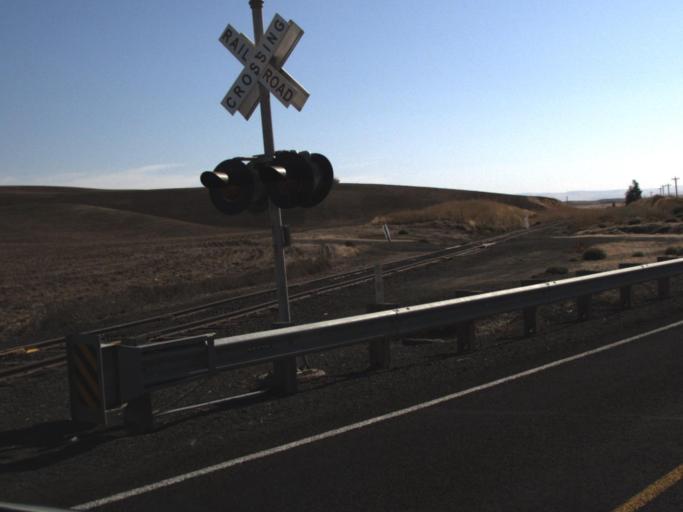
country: US
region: Washington
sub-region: Walla Walla County
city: Walla Walla
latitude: 46.1944
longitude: -118.3824
